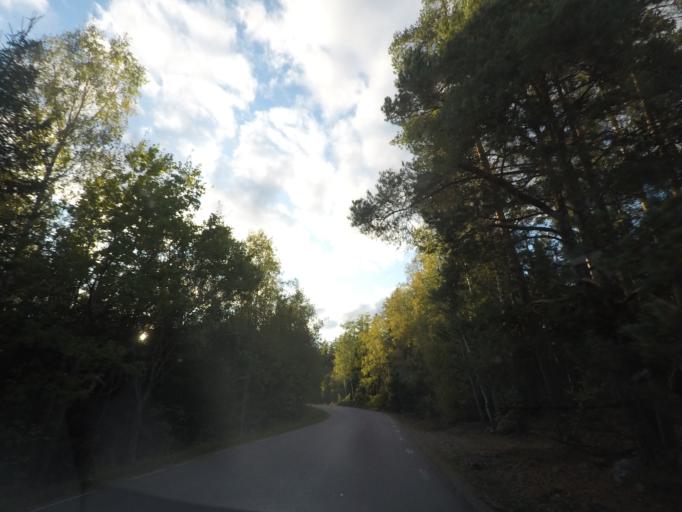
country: SE
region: Vaestmanland
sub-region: Kungsors Kommun
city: Kungsoer
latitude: 59.5096
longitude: 16.0821
